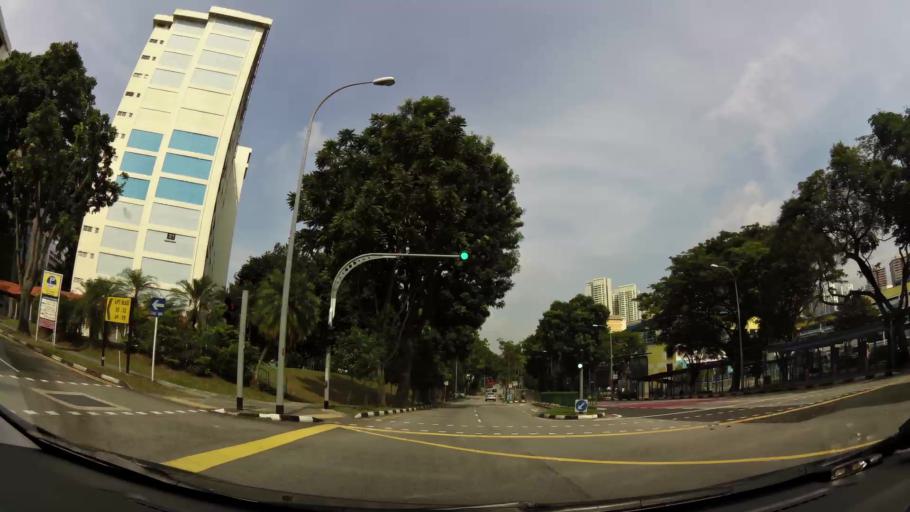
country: SG
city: Singapore
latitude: 1.3004
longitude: 103.7843
